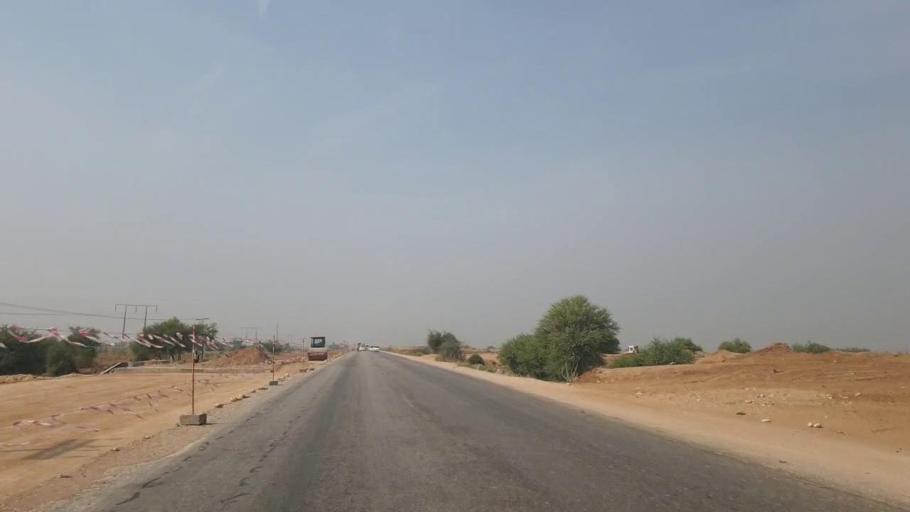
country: PK
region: Sindh
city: Sann
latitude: 26.1226
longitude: 68.0577
